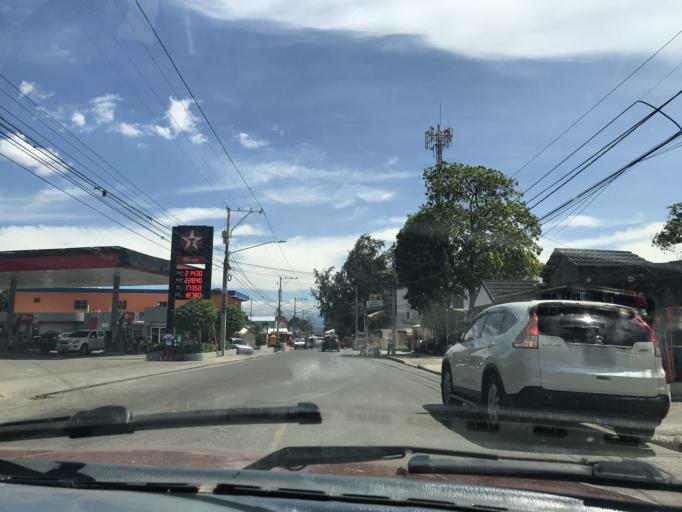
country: DO
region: Santiago
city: Tamboril
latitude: 19.4964
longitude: -70.6526
